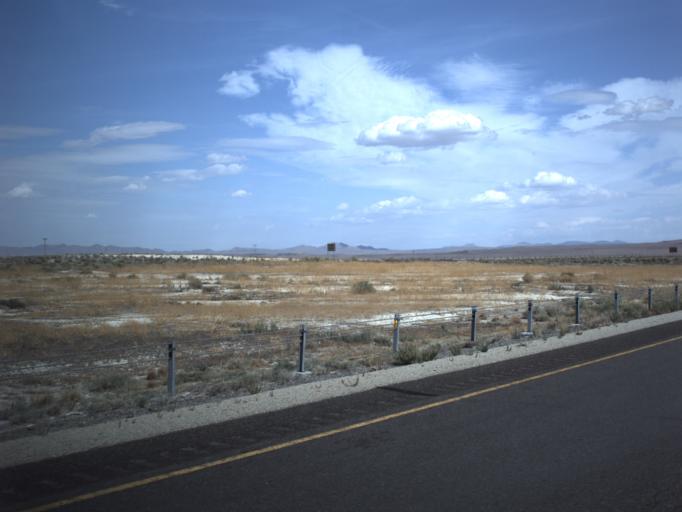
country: US
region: Utah
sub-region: Tooele County
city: Wendover
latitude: 40.7264
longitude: -113.2569
